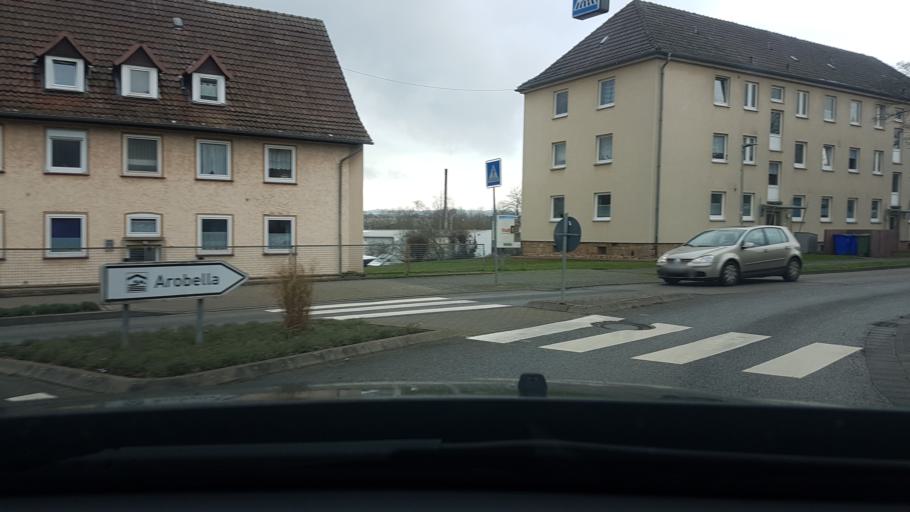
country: DE
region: Hesse
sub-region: Regierungsbezirk Kassel
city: Bad Arolsen
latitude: 51.3764
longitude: 9.0129
